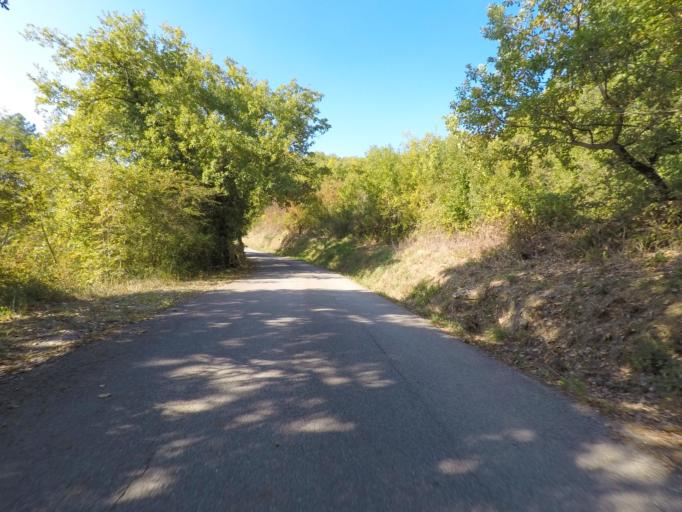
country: IT
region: Tuscany
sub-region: Provincia di Siena
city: Castellina in Chianti
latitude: 43.4320
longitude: 11.3390
